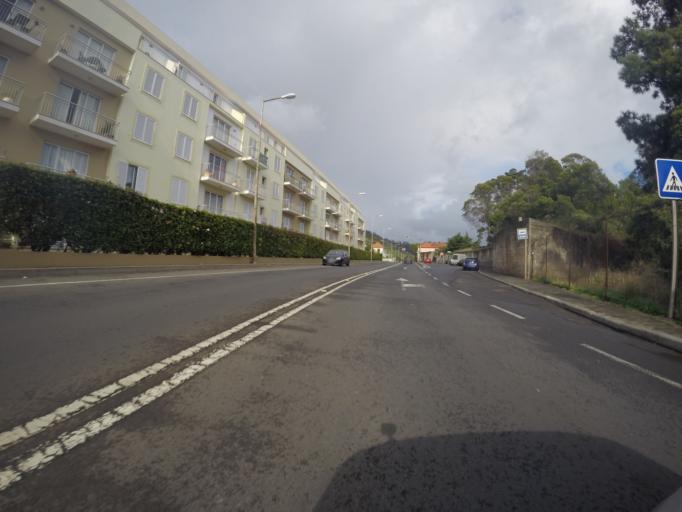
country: PT
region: Madeira
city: Canico
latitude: 32.6493
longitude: -16.8529
